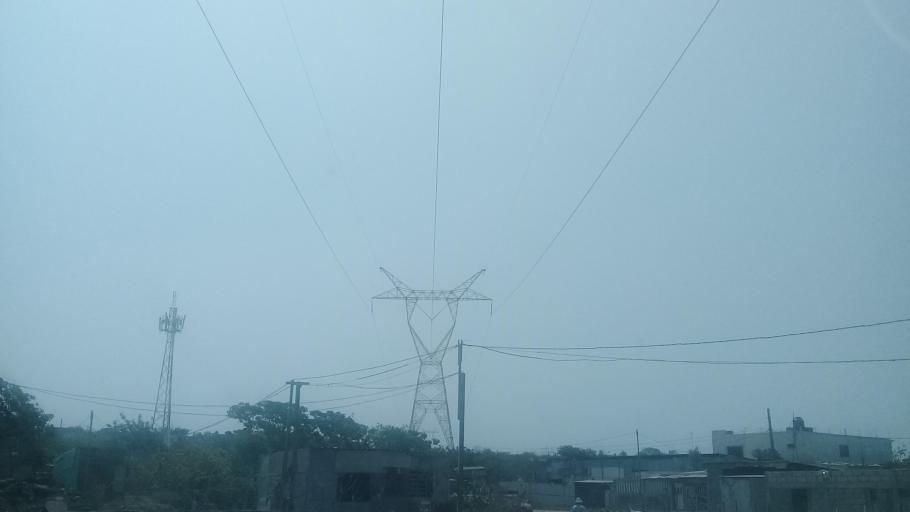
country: MX
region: Veracruz
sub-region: Veracruz
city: Las Amapolas
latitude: 19.1688
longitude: -96.1790
